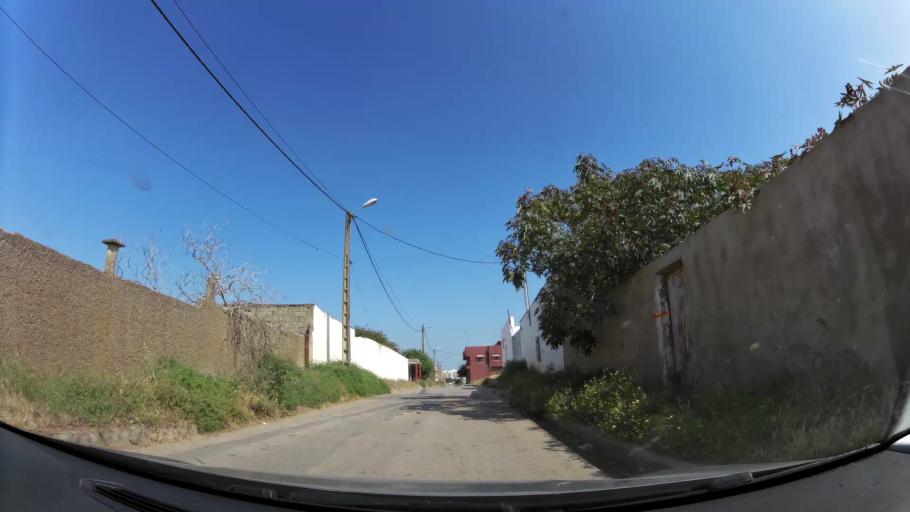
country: MA
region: Rabat-Sale-Zemmour-Zaer
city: Sale
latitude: 34.0731
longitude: -6.7617
